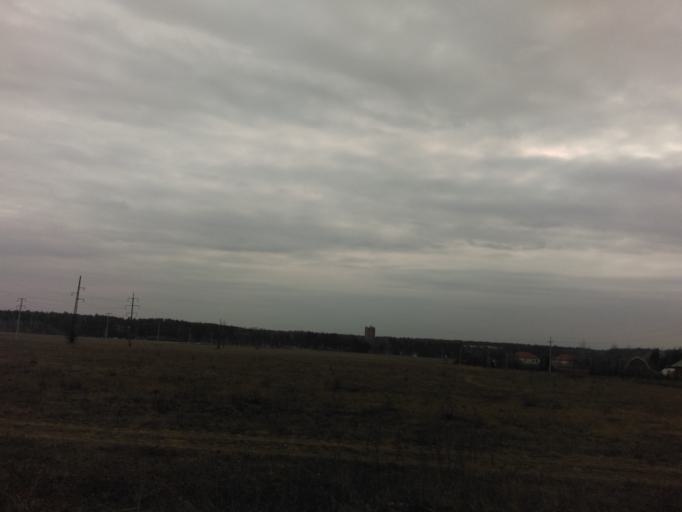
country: RU
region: Moskovskaya
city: Zvenigorod
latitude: 55.7350
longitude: 36.9481
